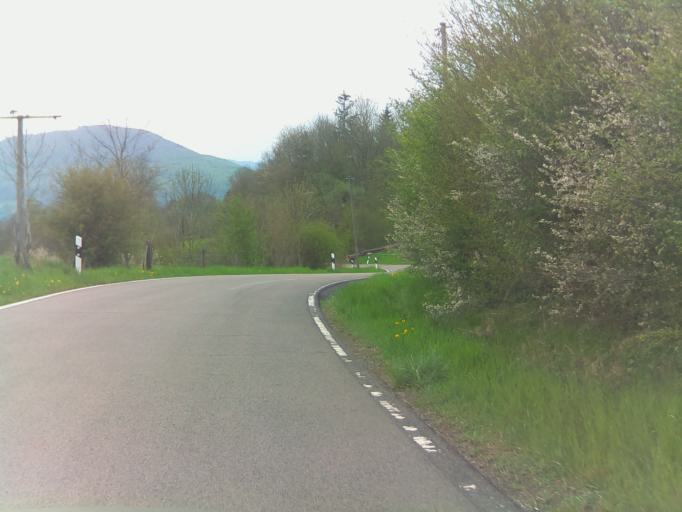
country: DE
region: Thuringia
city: Unterweid
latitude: 50.6276
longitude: 10.0547
